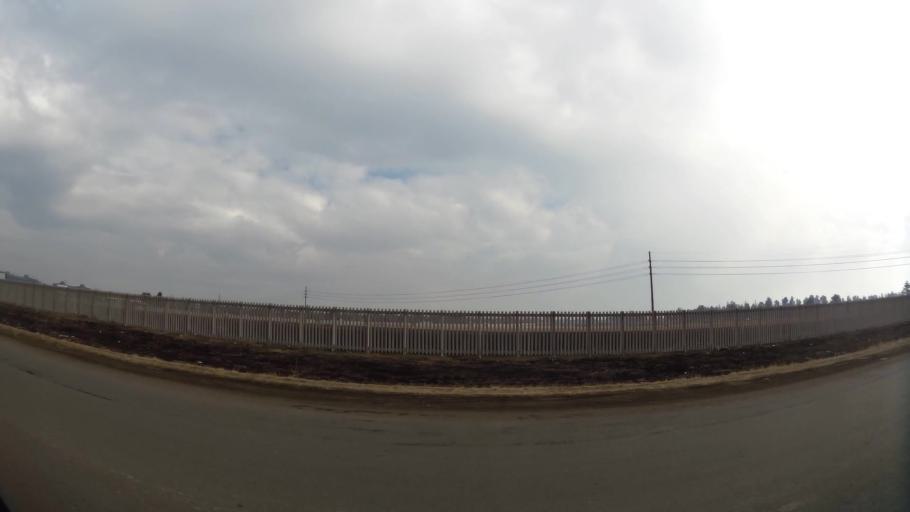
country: ZA
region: Gauteng
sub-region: Sedibeng District Municipality
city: Vanderbijlpark
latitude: -26.6999
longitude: 27.8607
